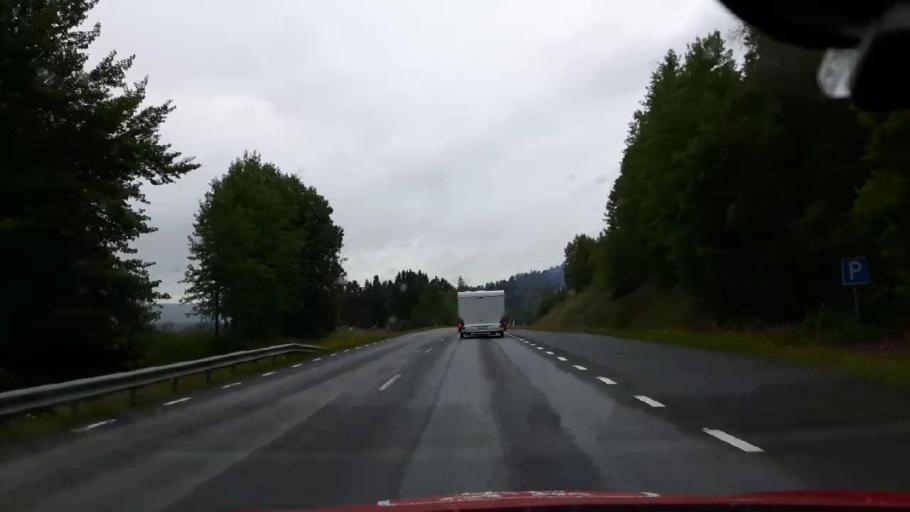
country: SE
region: Jaemtland
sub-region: Are Kommun
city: Jarpen
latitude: 63.3108
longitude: 13.6602
